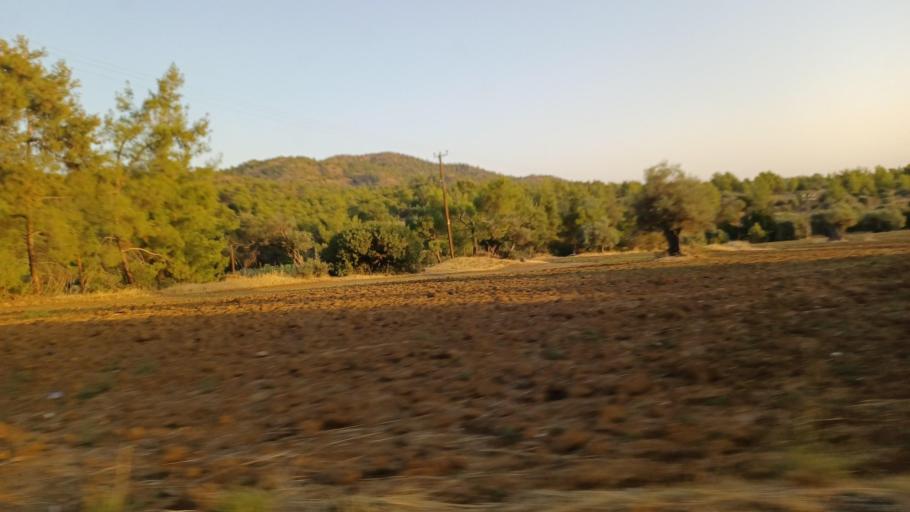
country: CY
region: Lefkosia
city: Lythrodontas
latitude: 34.9468
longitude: 33.2847
